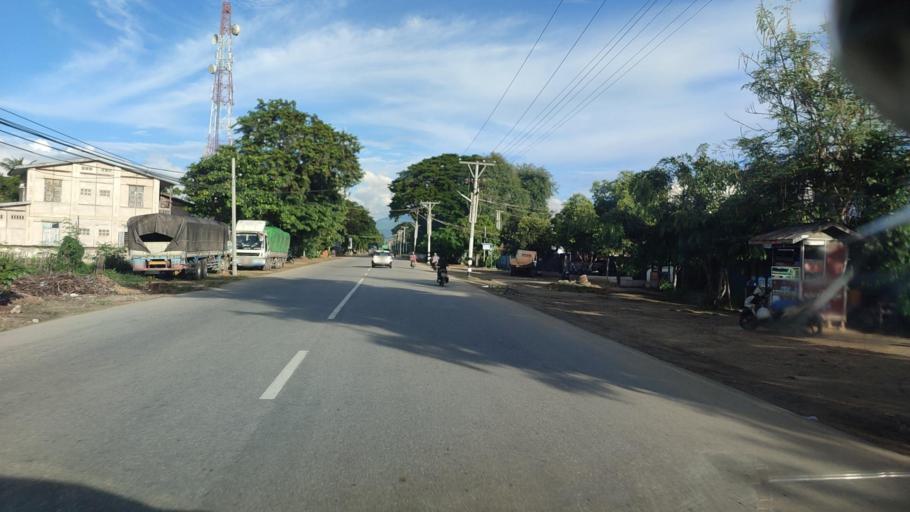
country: MM
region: Mandalay
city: Yamethin
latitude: 20.1245
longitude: 96.2086
